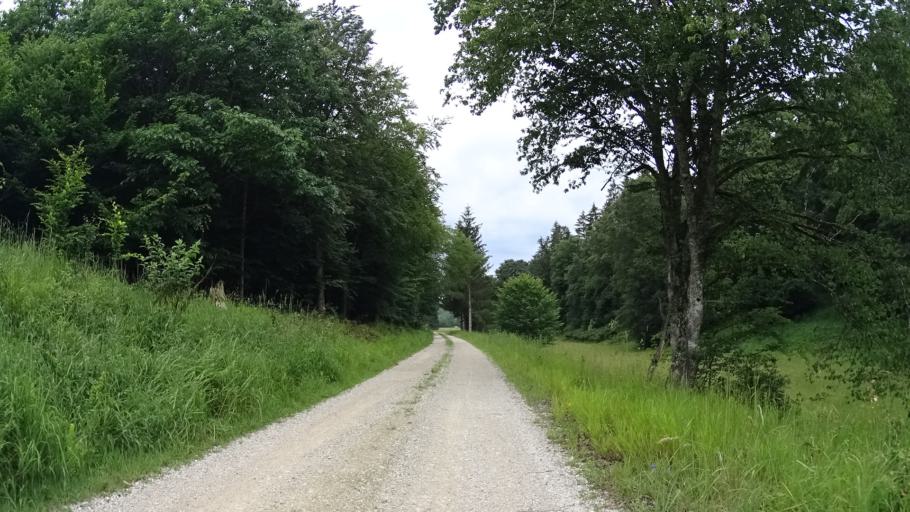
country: DE
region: Bavaria
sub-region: Upper Bavaria
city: Denkendorf
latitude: 48.9148
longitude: 11.5399
